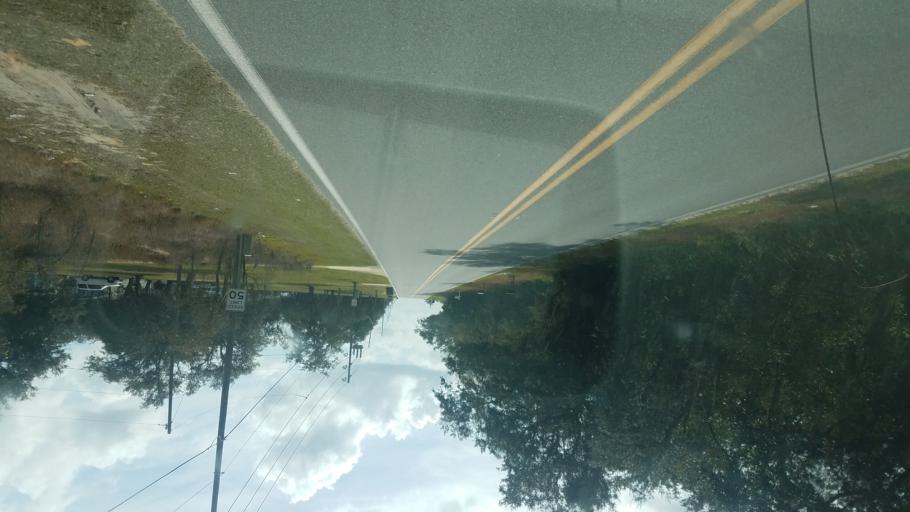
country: US
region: Florida
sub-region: Polk County
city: Dundee
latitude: 28.0336
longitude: -81.5293
